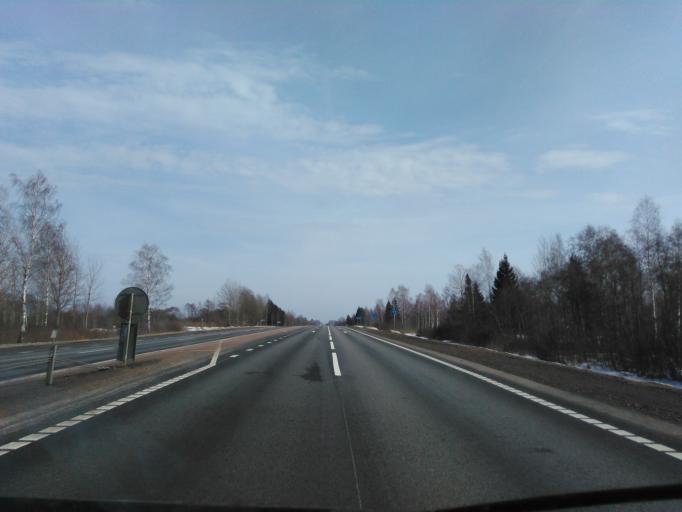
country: BY
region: Vitebsk
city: Dubrowna
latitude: 54.6897
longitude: 30.9170
